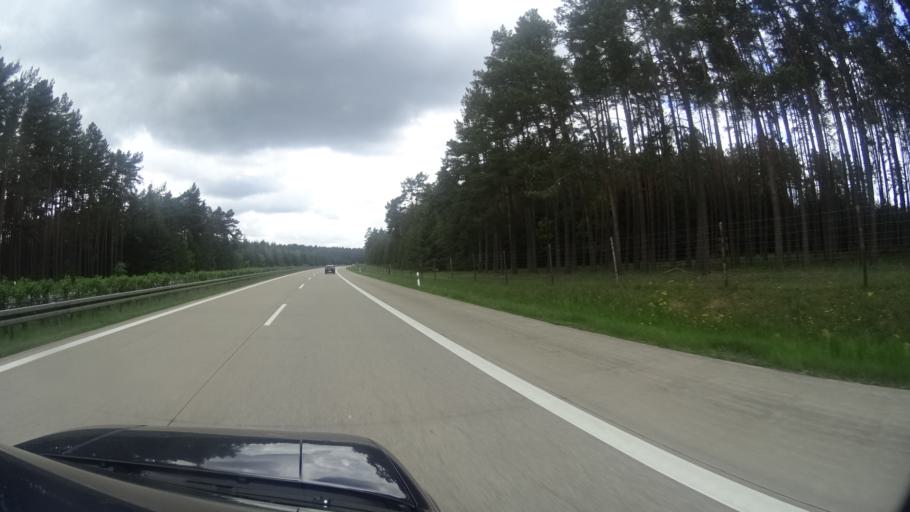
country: DE
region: Mecklenburg-Vorpommern
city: Plau am See
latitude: 53.5521
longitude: 12.3232
